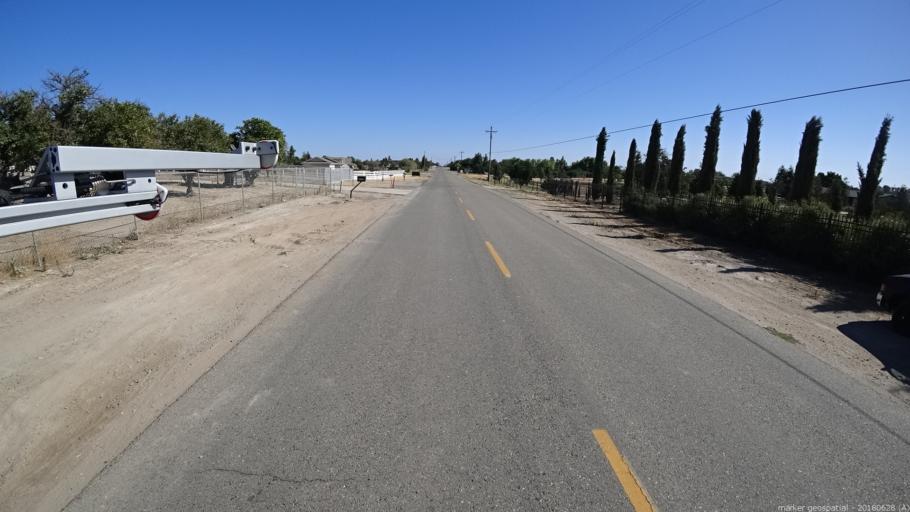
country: US
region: California
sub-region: Madera County
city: Bonadelle Ranchos-Madera Ranchos
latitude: 36.9822
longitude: -119.8794
